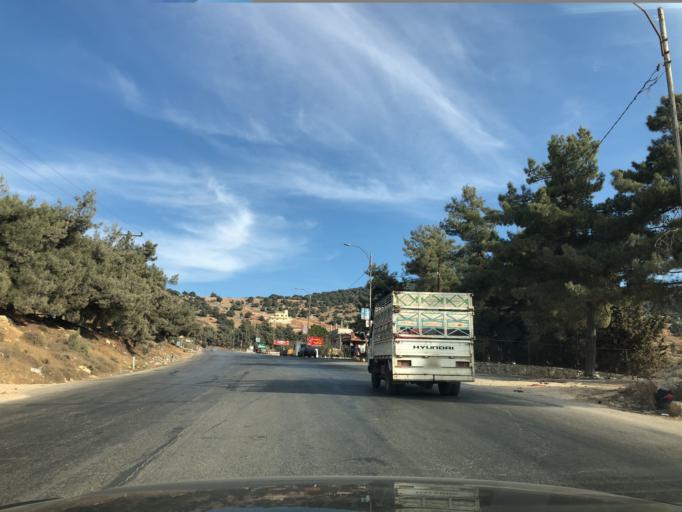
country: JO
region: Irbid
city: `Anjarah
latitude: 32.3132
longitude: 35.7750
